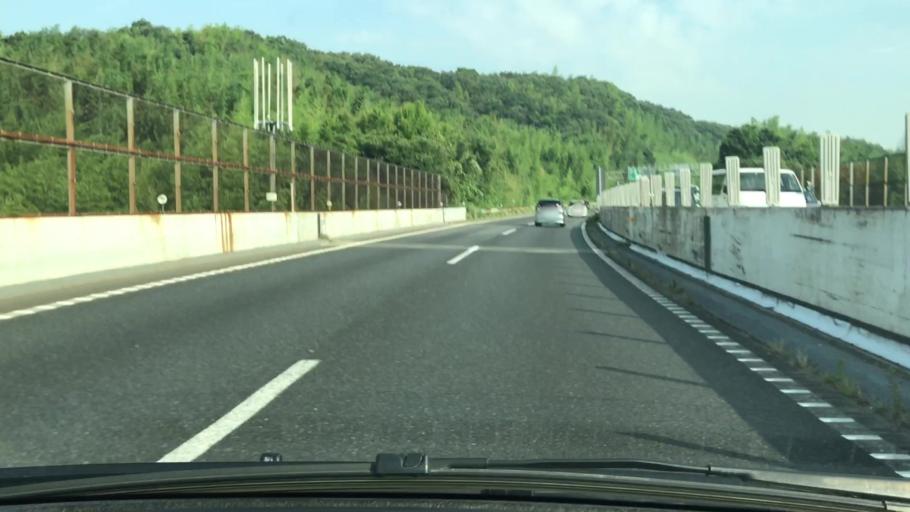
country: JP
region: Hyogo
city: Akashi
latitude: 34.6895
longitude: 134.9715
